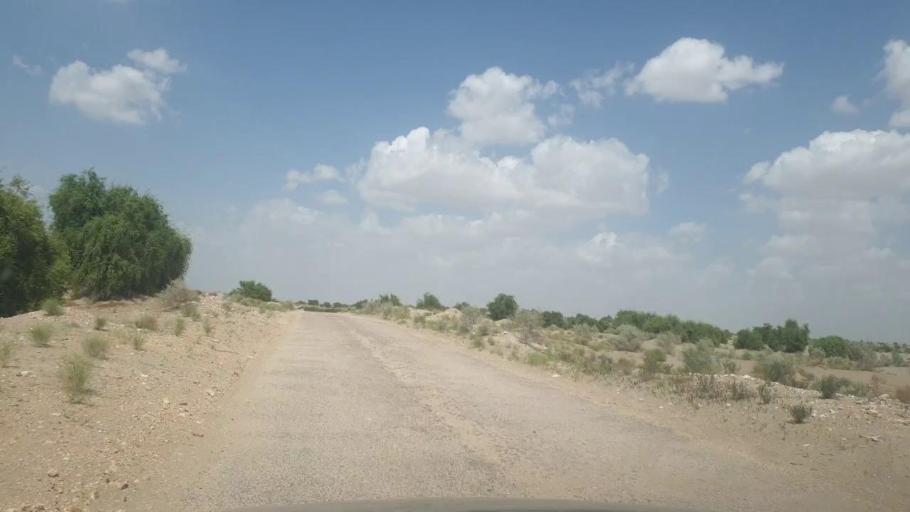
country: PK
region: Sindh
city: Kot Diji
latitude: 27.2303
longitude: 69.1174
